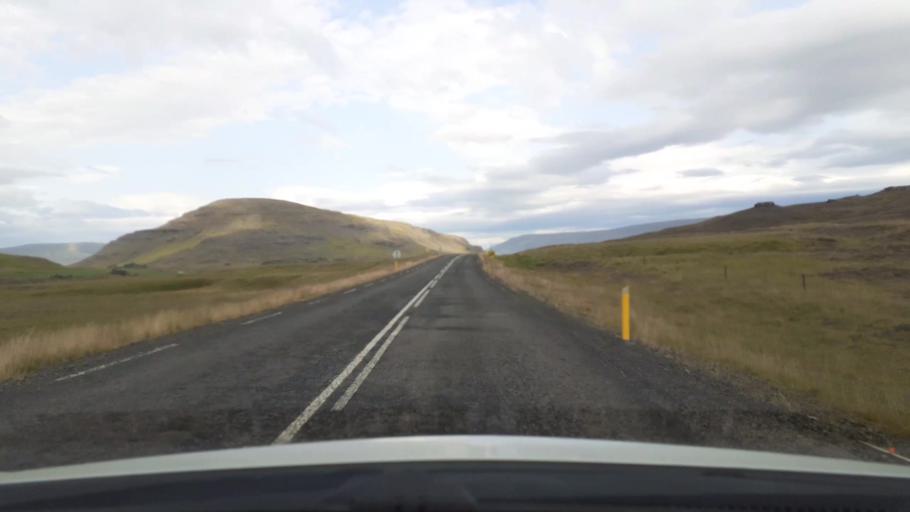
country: IS
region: Capital Region
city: Mosfellsbaer
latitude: 64.3007
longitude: -21.4829
